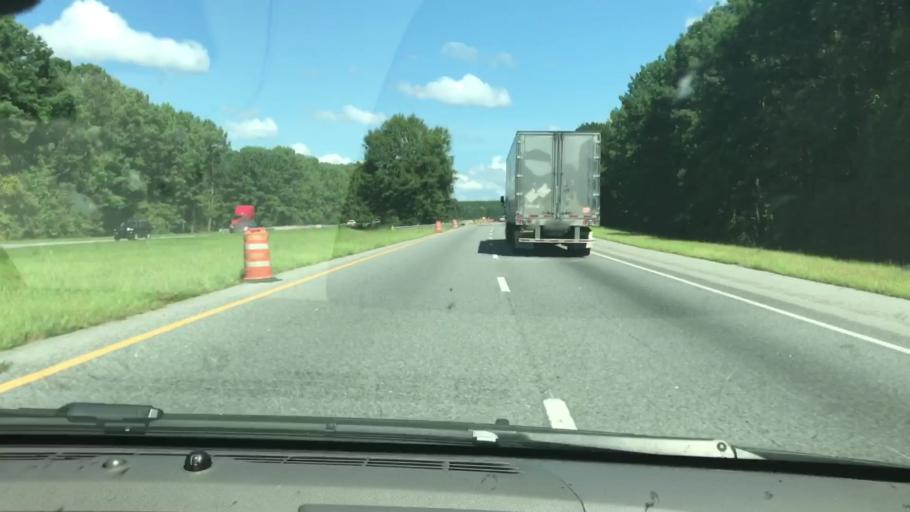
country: US
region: Georgia
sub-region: Harris County
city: Hamilton
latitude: 32.7052
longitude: -85.0098
